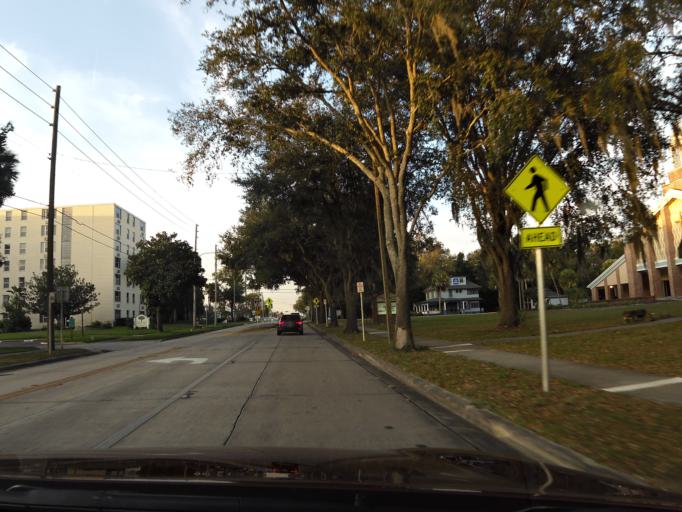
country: US
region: Florida
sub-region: Volusia County
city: North DeLand
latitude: 29.0400
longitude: -81.3038
